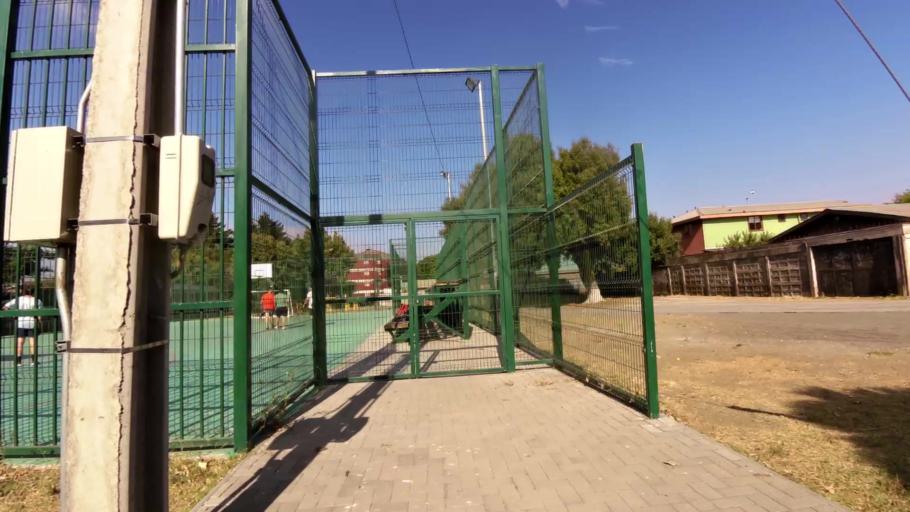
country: CL
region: Biobio
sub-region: Provincia de Concepcion
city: Concepcion
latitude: -36.7974
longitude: -73.0878
